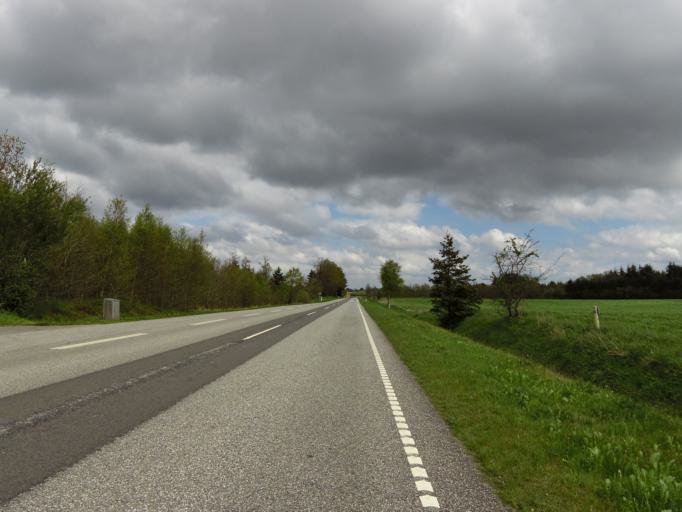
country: DK
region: South Denmark
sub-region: Haderslev Kommune
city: Gram
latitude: 55.2637
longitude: 8.9960
